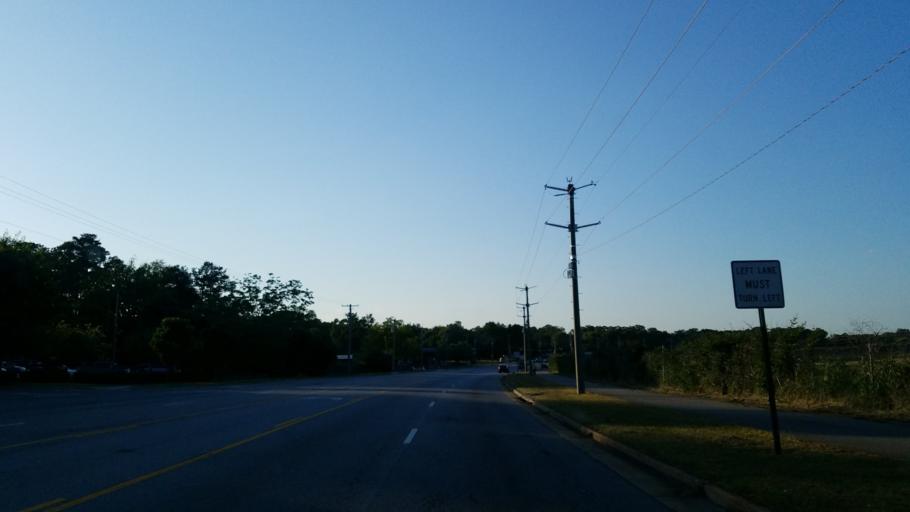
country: US
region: Georgia
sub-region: Cobb County
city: Fair Oaks
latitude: 33.9192
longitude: -84.5418
